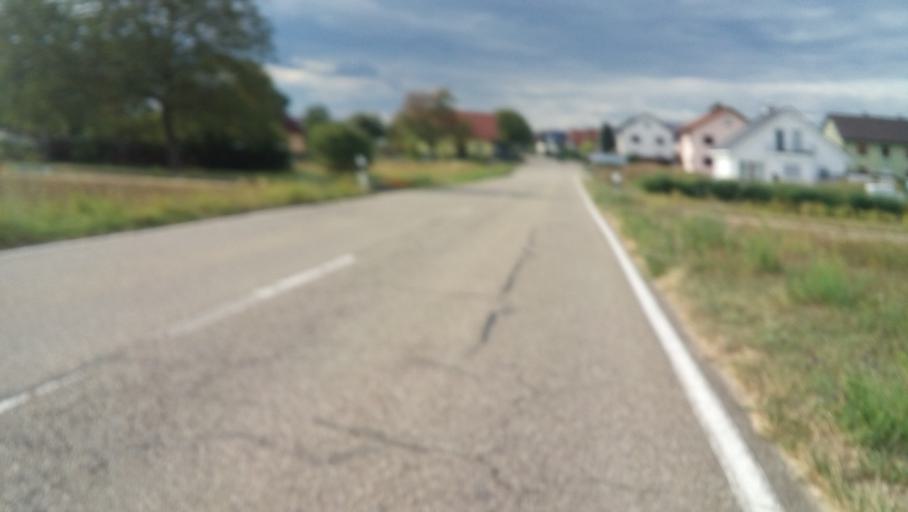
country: DE
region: Baden-Wuerttemberg
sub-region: Karlsruhe Region
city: Schwarzach
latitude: 48.7654
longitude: 8.0542
